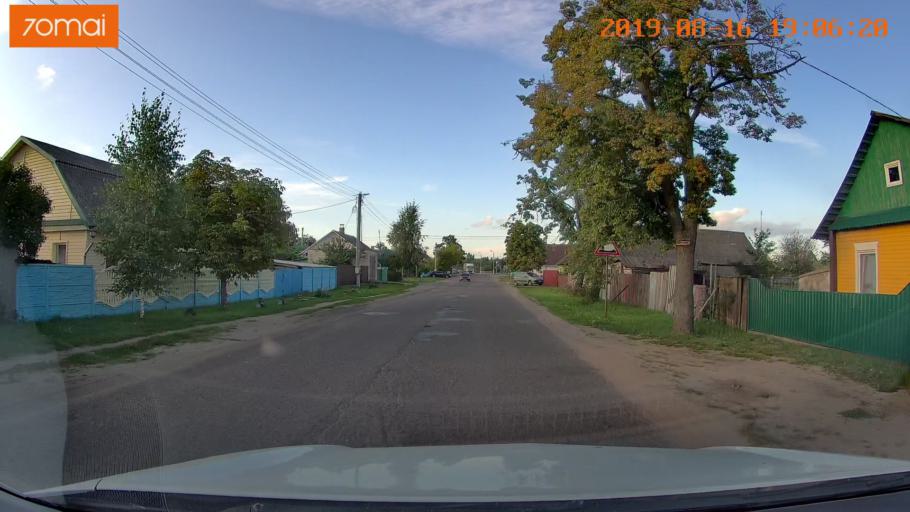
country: BY
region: Mogilev
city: Asipovichy
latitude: 53.2995
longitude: 28.6217
